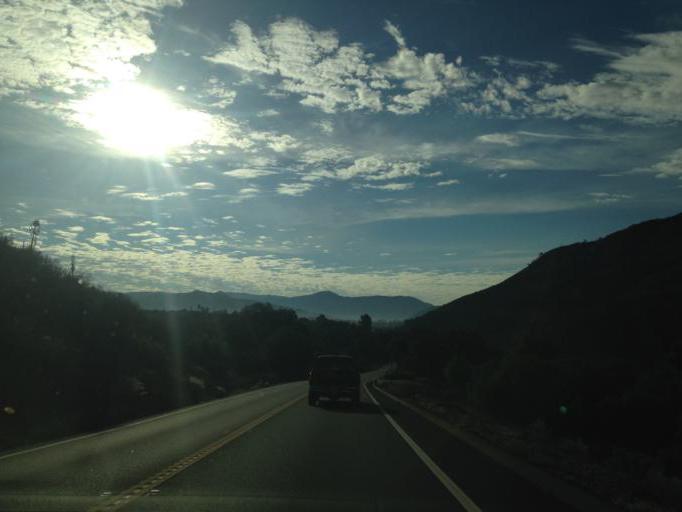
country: US
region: California
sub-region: San Diego County
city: Valley Center
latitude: 33.3475
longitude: -117.0248
